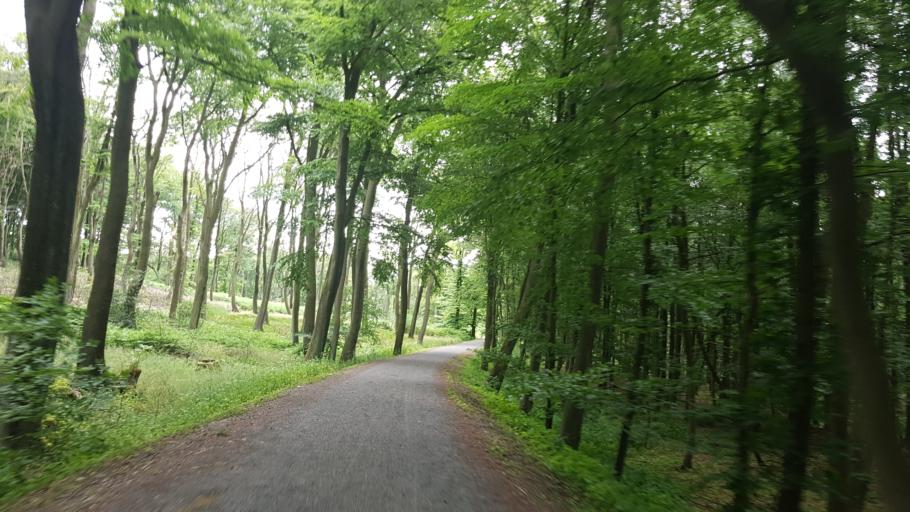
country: DE
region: North Rhine-Westphalia
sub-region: Regierungsbezirk Dusseldorf
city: Muelheim (Ruhr)
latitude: 51.4002
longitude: 6.8262
